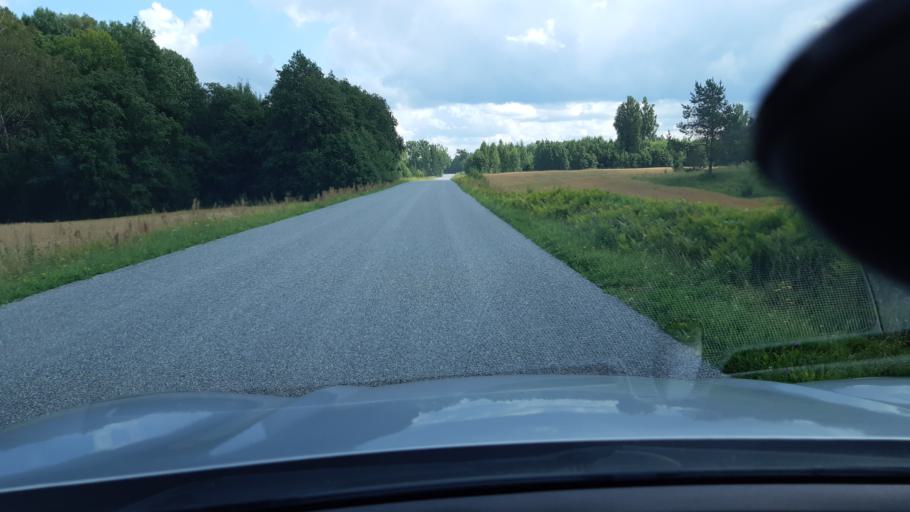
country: EE
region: Raplamaa
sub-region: Kehtna vald
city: Kehtna
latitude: 58.9068
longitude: 25.0510
